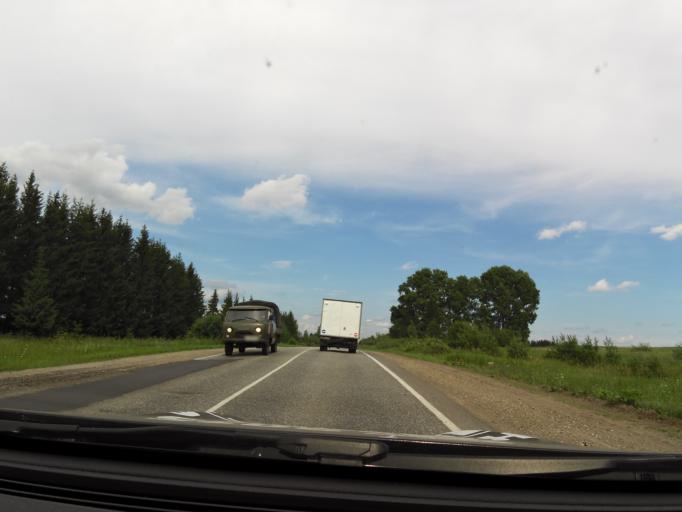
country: RU
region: Kirov
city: Stulovo
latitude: 58.7081
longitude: 50.1016
